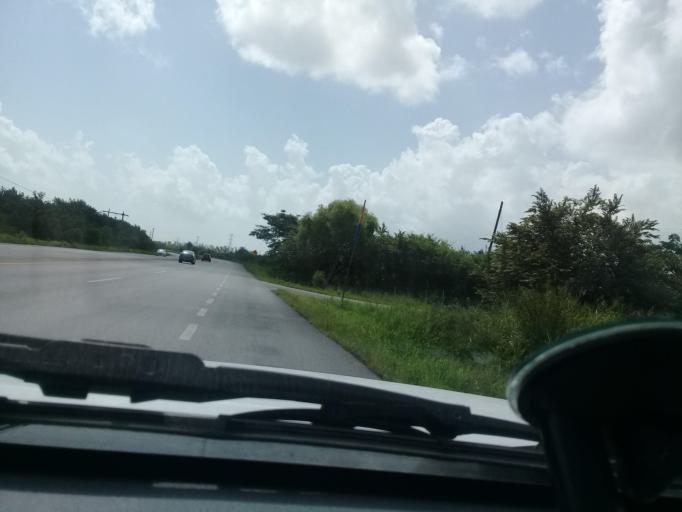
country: MX
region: Veracruz
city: Moralillo
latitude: 22.2120
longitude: -97.9655
